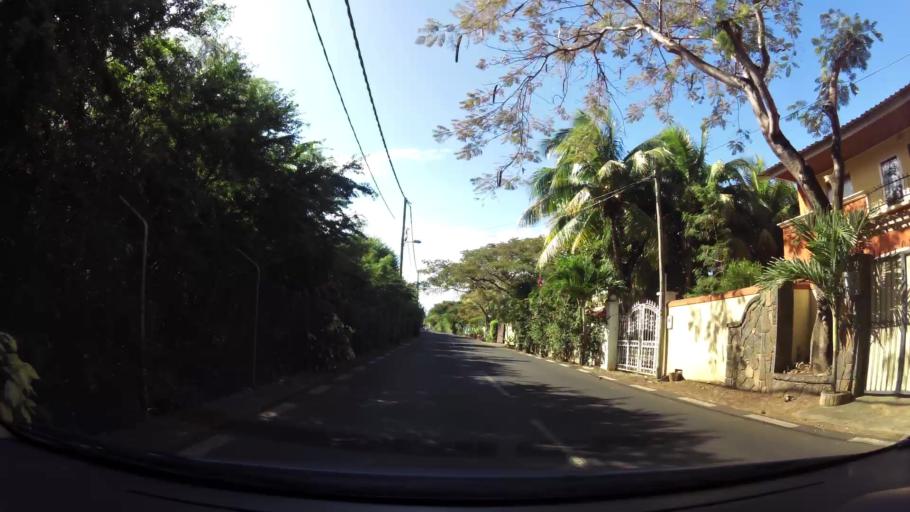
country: MU
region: Black River
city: Albion
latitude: -20.2164
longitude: 57.4037
